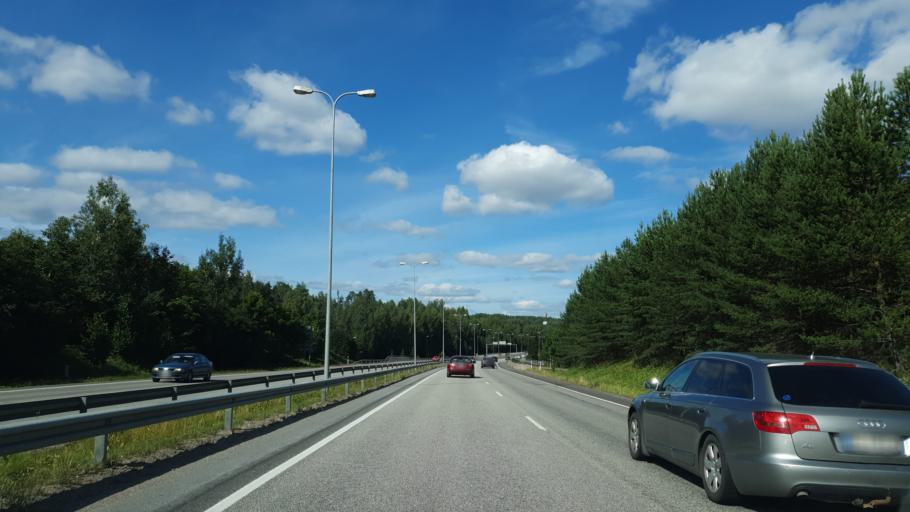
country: FI
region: Central Finland
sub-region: Jyvaeskylae
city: Jyvaeskylae
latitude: 62.2244
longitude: 25.7263
